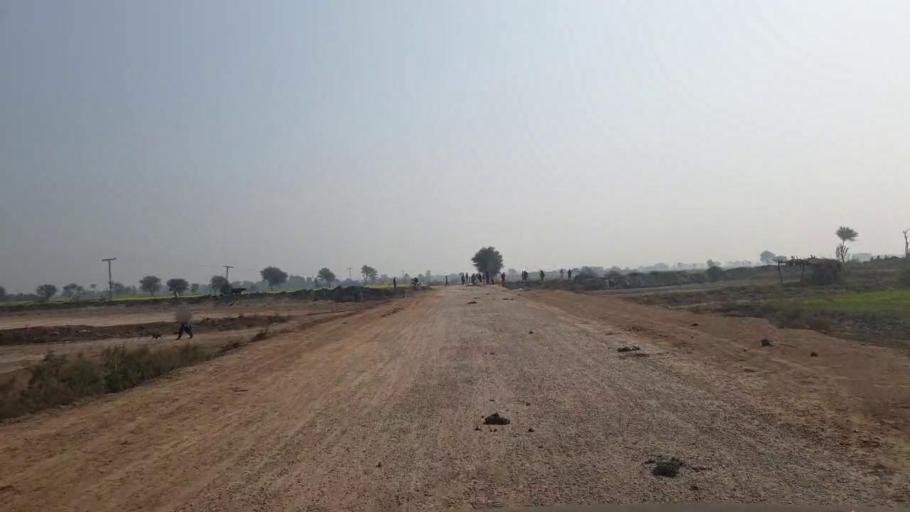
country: PK
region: Sindh
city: Hala
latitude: 25.9408
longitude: 68.4468
